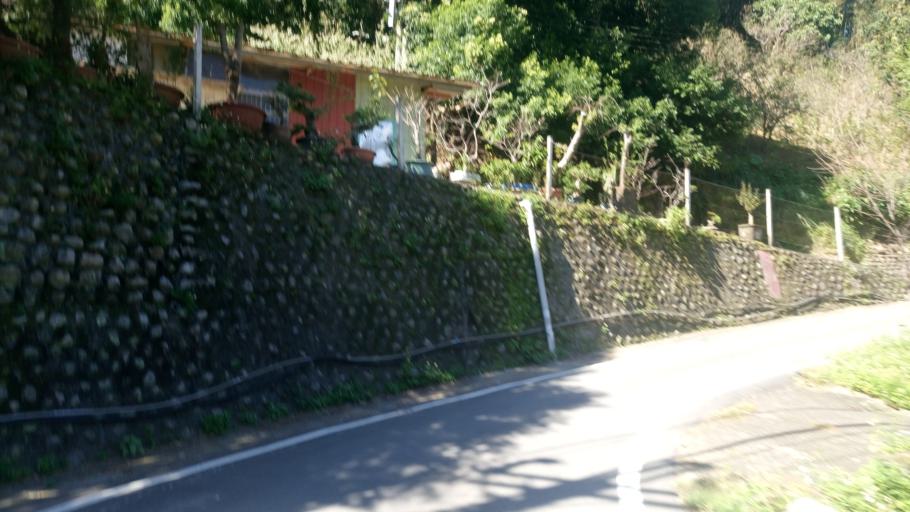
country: TW
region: Taiwan
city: Daxi
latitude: 24.7019
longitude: 121.1806
